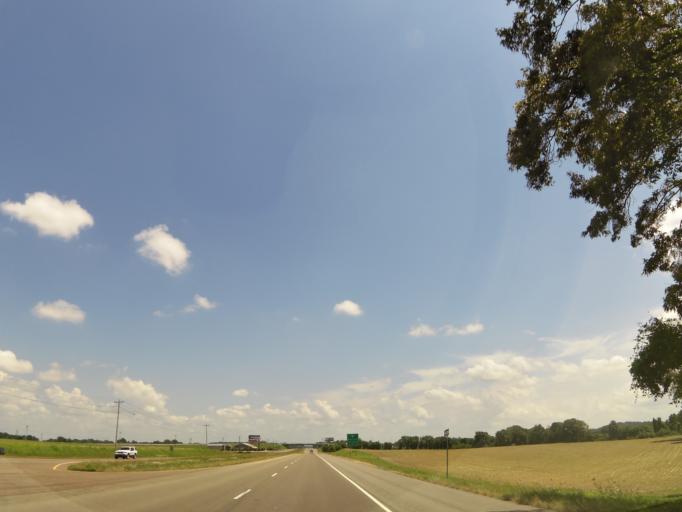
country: US
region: Tennessee
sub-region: Crockett County
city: Alamo
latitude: 35.8889
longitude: -89.2336
